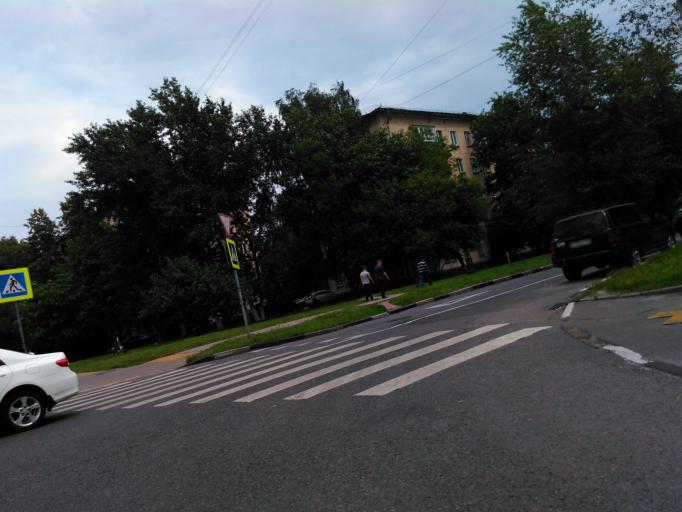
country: RU
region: Moscow
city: Novyye Cheremushki
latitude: 55.6904
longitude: 37.5805
